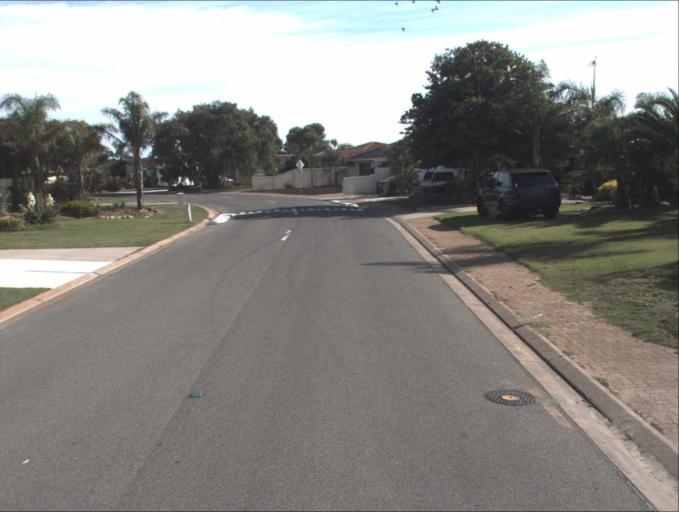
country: AU
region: South Australia
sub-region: Port Adelaide Enfield
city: Birkenhead
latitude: -34.7897
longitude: 138.4954
